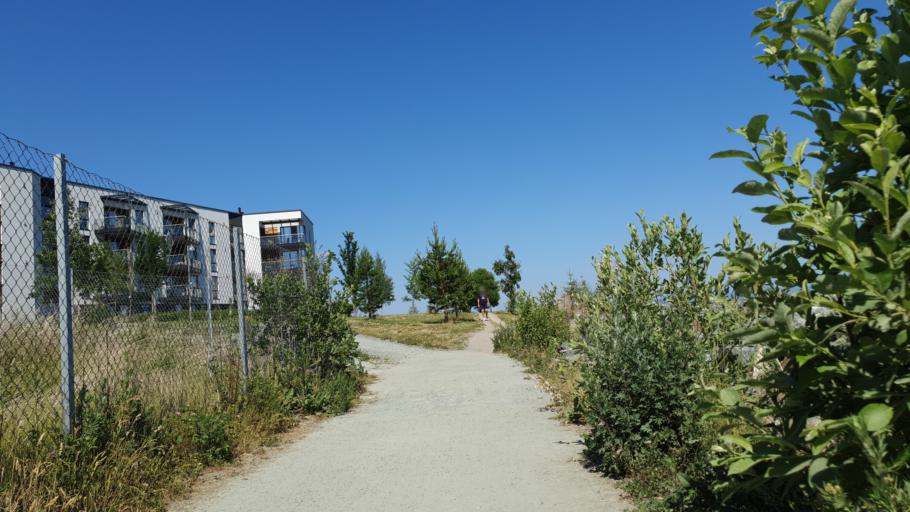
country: NO
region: Sor-Trondelag
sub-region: Trondheim
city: Trondheim
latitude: 63.4346
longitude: 10.5114
